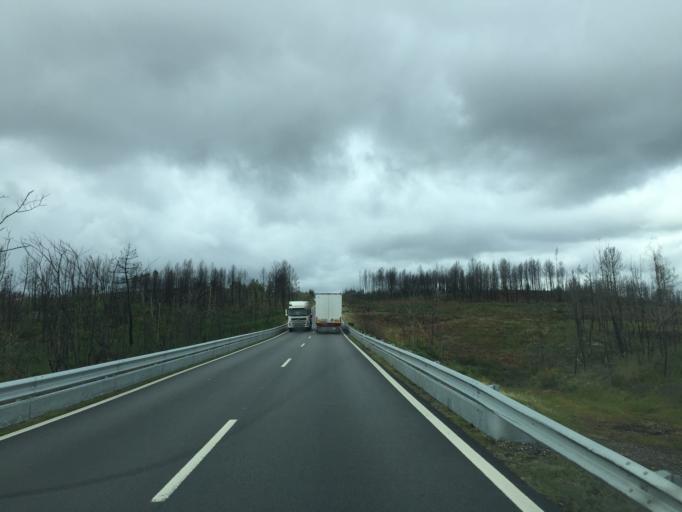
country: PT
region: Coimbra
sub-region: Oliveira do Hospital
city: Oliveira do Hospital
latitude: 40.3206
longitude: -7.9155
